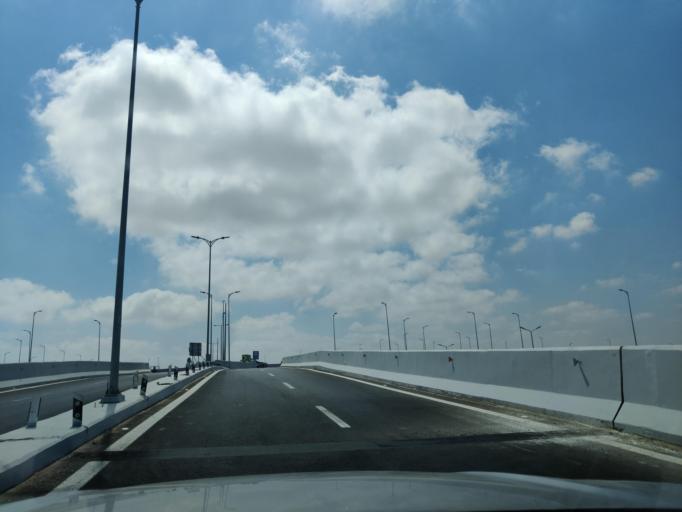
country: EG
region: Muhafazat Matruh
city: Al `Alamayn
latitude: 30.8246
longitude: 28.9843
